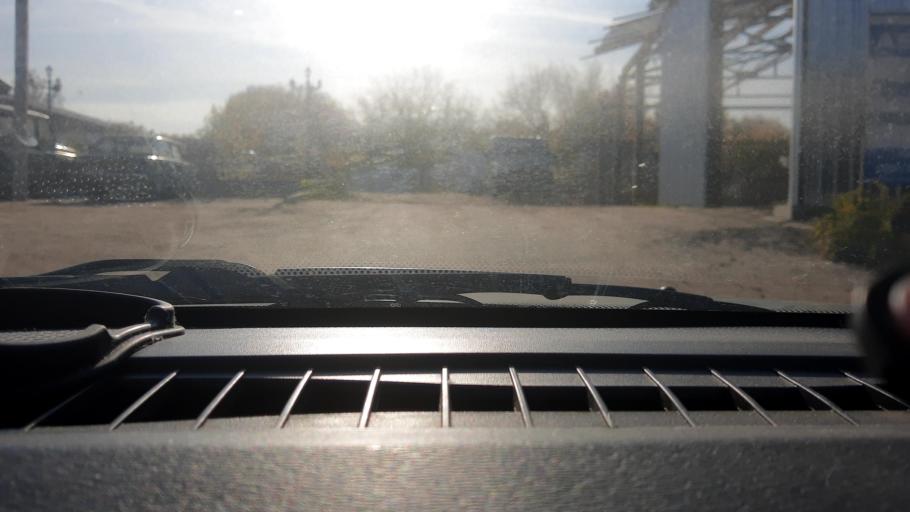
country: RU
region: Nizjnij Novgorod
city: Afonino
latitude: 56.2318
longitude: 44.0938
